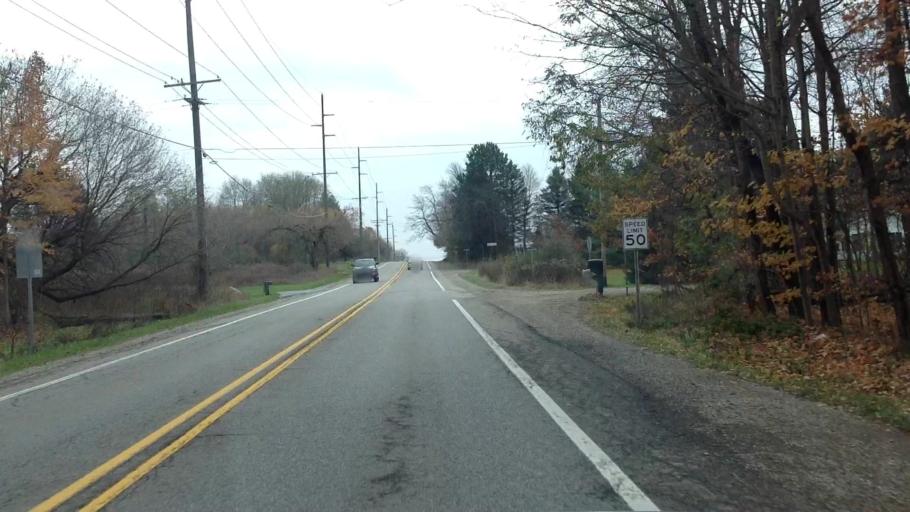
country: US
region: Michigan
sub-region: Oakland County
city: Milford
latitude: 42.6148
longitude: -83.6605
